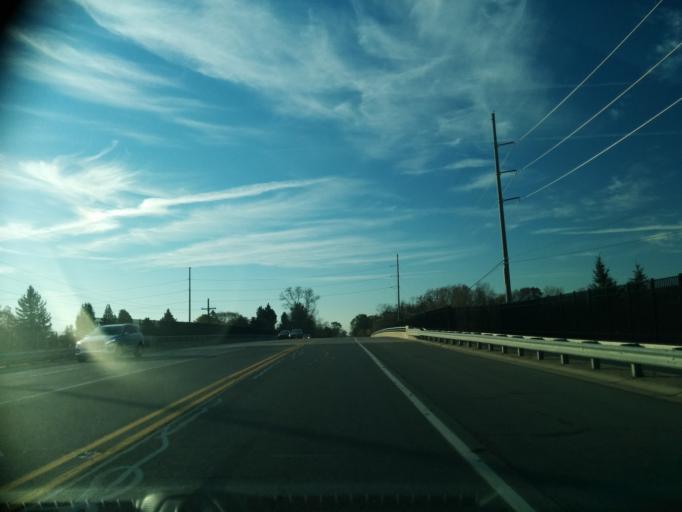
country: US
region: Michigan
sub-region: Oakland County
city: Farmington Hills
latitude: 42.4925
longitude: -83.4171
